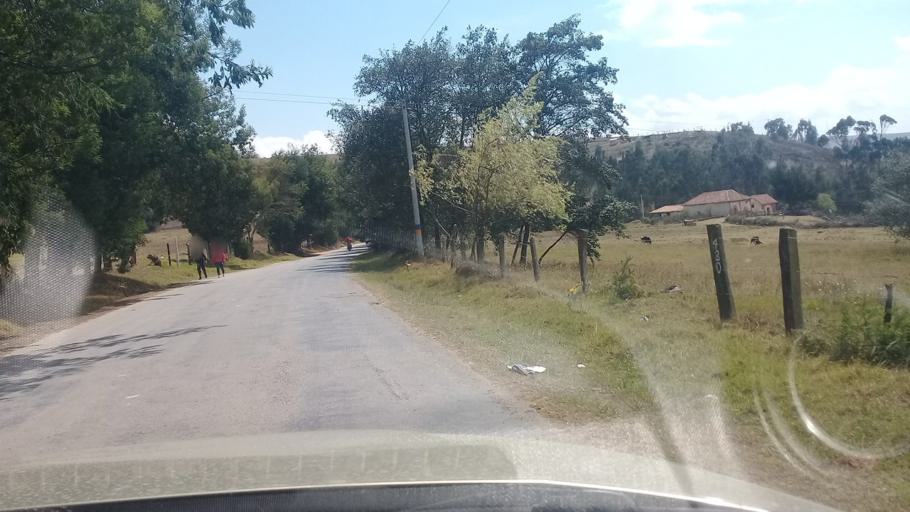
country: CO
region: Boyaca
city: Siachoque
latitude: 5.5526
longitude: -73.2873
